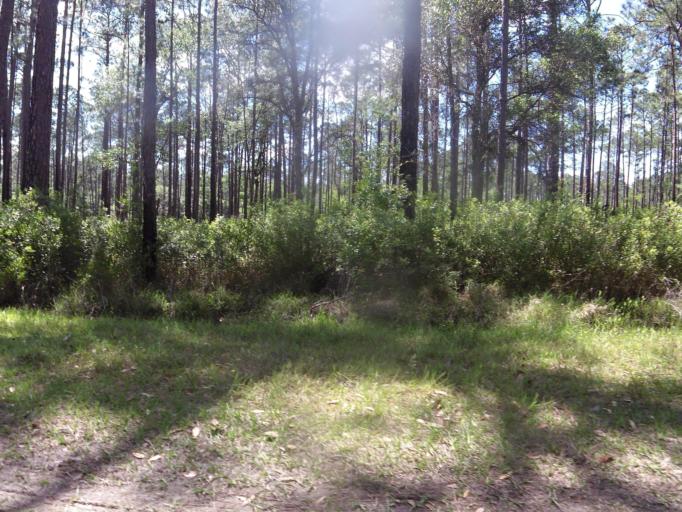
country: US
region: Florida
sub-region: Clay County
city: Green Cove Springs
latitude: 29.9621
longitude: -81.6317
